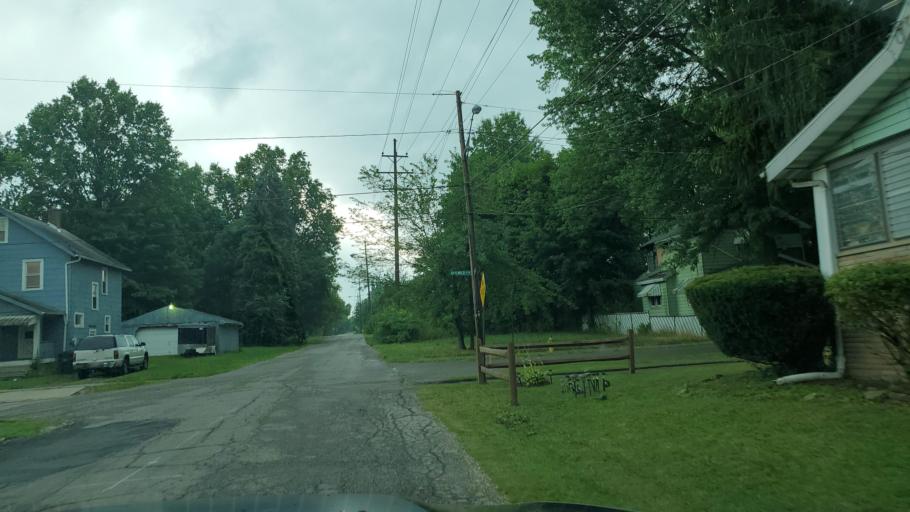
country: US
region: Ohio
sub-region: Trumbull County
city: Warren
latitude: 41.2526
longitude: -80.8134
